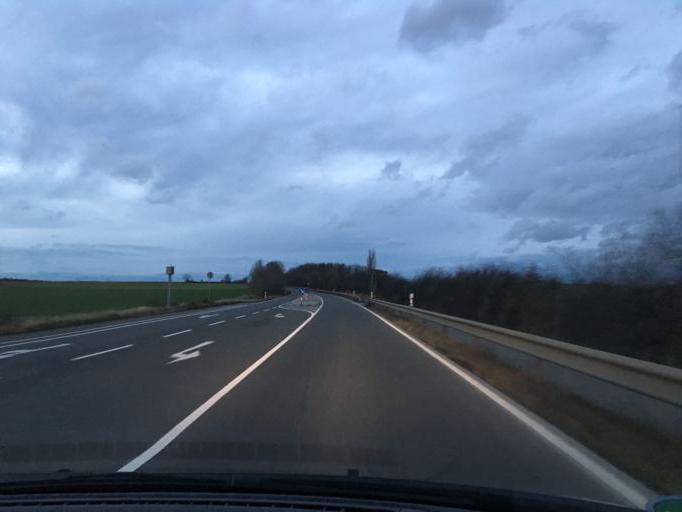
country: DE
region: North Rhine-Westphalia
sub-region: Regierungsbezirk Koln
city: Vettweiss
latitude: 50.6997
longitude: 6.6060
